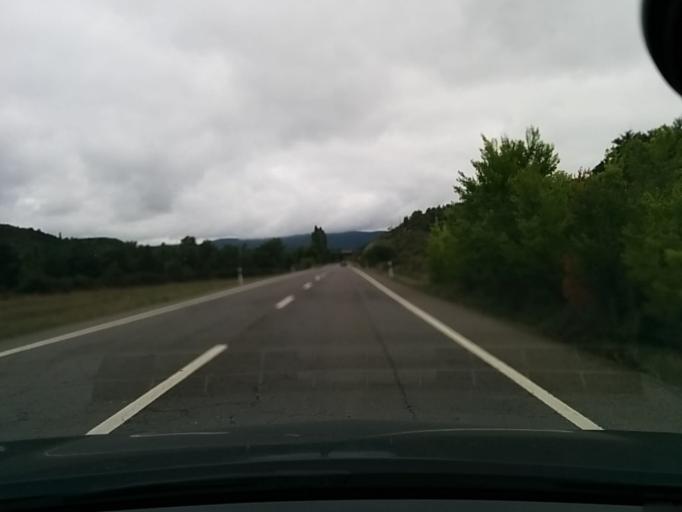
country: ES
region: Aragon
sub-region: Provincia de Huesca
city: Sabinanigo
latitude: 42.4514
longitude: -0.3906
